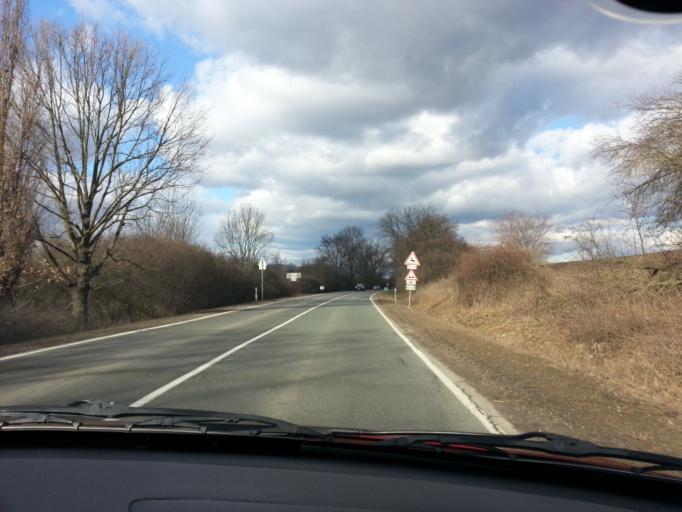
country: HU
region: Nograd
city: Szurdokpuspoki
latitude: 47.8760
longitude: 19.6722
